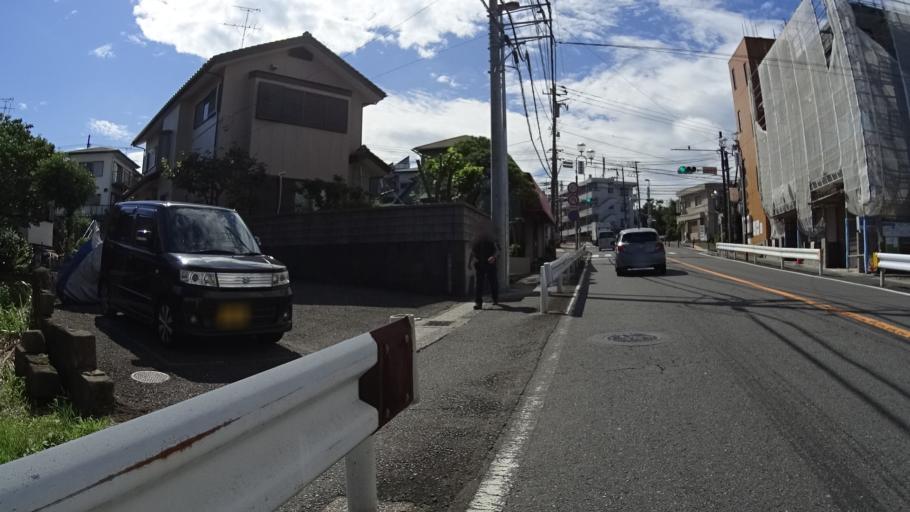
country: JP
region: Kanagawa
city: Yokosuka
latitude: 35.2593
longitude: 139.7058
